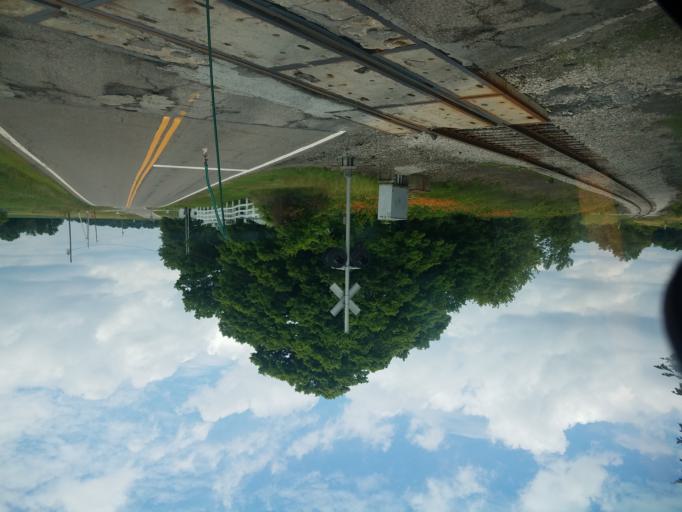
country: US
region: Ohio
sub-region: Huron County
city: Plymouth
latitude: 40.9582
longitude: -82.6877
